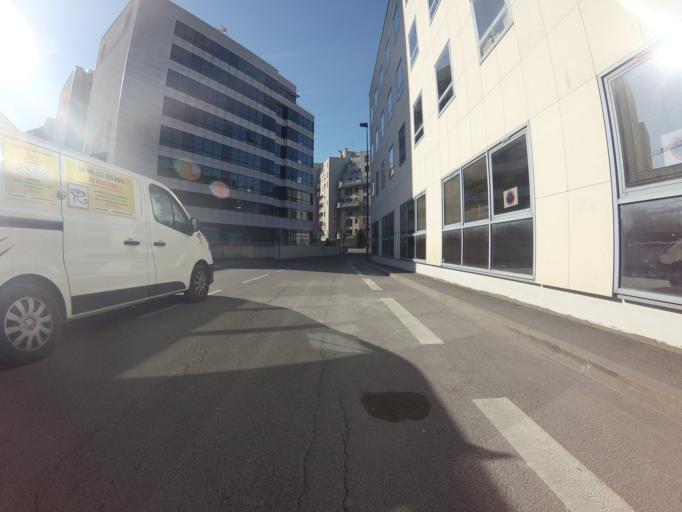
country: FR
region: Ile-de-France
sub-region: Departement des Hauts-de-Seine
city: Clichy
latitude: 48.9049
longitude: 2.3192
